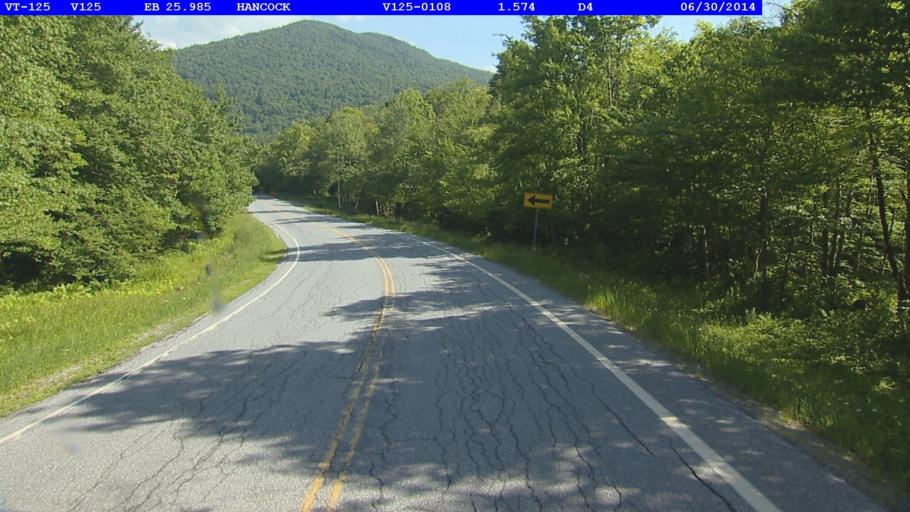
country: US
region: Vermont
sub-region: Rutland County
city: Brandon
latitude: 43.9305
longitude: -72.9466
